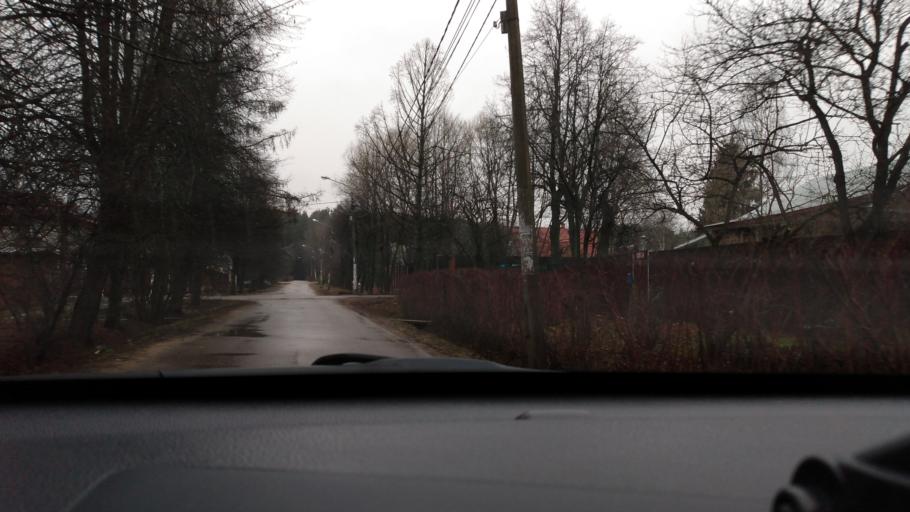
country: RU
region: Moskovskaya
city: Lesnoy Gorodok
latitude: 55.6618
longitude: 37.1776
